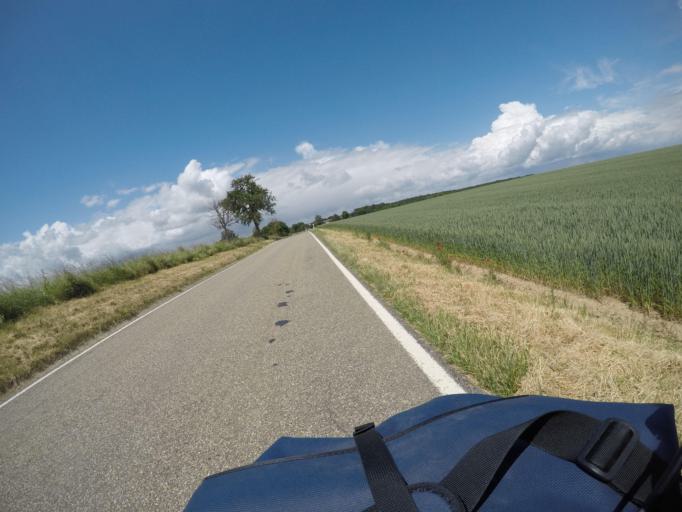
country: DE
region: Baden-Wuerttemberg
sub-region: Regierungsbezirk Stuttgart
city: Ittlingen
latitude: 49.1854
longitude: 8.9115
